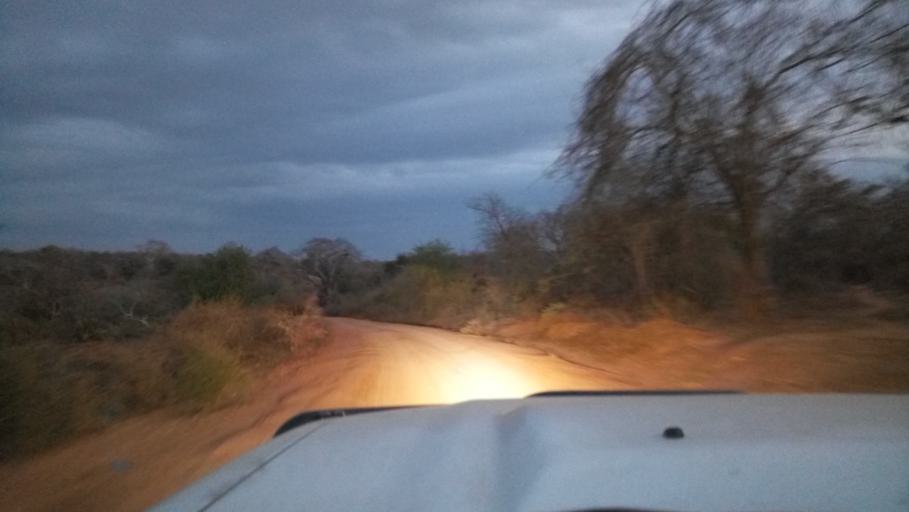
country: KE
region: Kitui
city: Kitui
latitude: -1.8027
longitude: 38.1897
